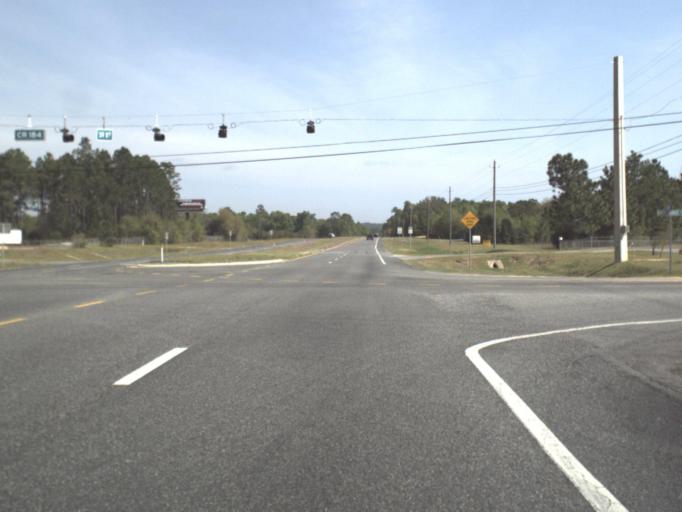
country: US
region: Florida
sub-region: Santa Rosa County
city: East Milton
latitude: 30.5955
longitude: -86.9414
